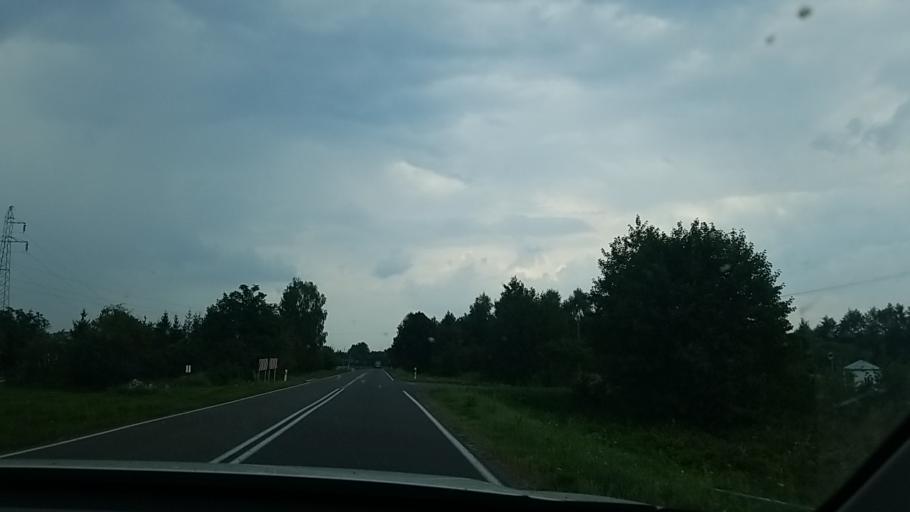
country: PL
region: Lublin Voivodeship
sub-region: Powiat leczynski
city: Cycow
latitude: 51.2377
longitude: 23.0867
